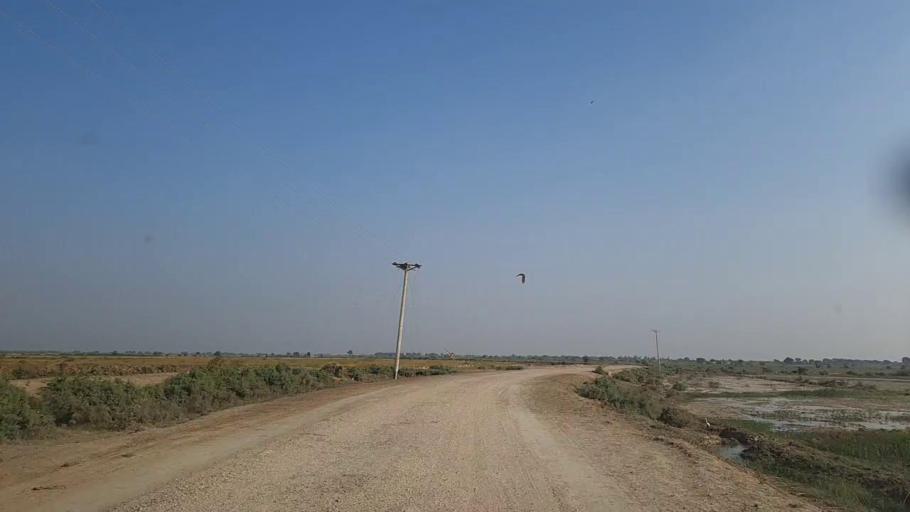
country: PK
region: Sindh
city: Jati
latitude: 24.4615
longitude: 68.2835
